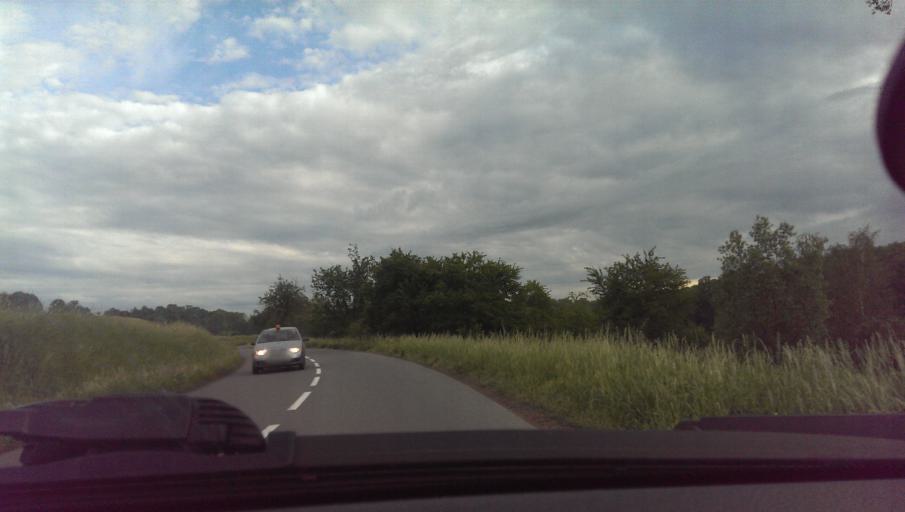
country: CZ
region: Zlin
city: Kvasice
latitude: 49.2265
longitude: 17.4899
